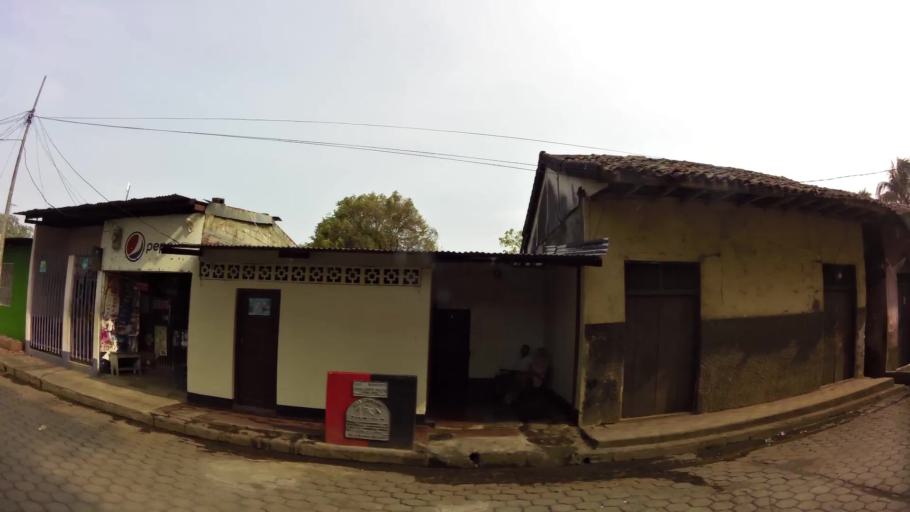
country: NI
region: Masaya
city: Masaya
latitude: 11.9677
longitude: -86.0931
